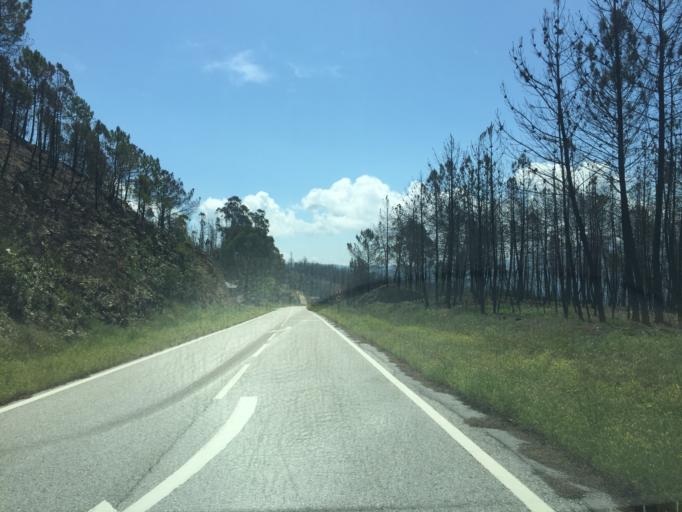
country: PT
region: Coimbra
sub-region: Pampilhosa da Serra
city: Pampilhosa da Serra
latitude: 40.0066
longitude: -7.9807
